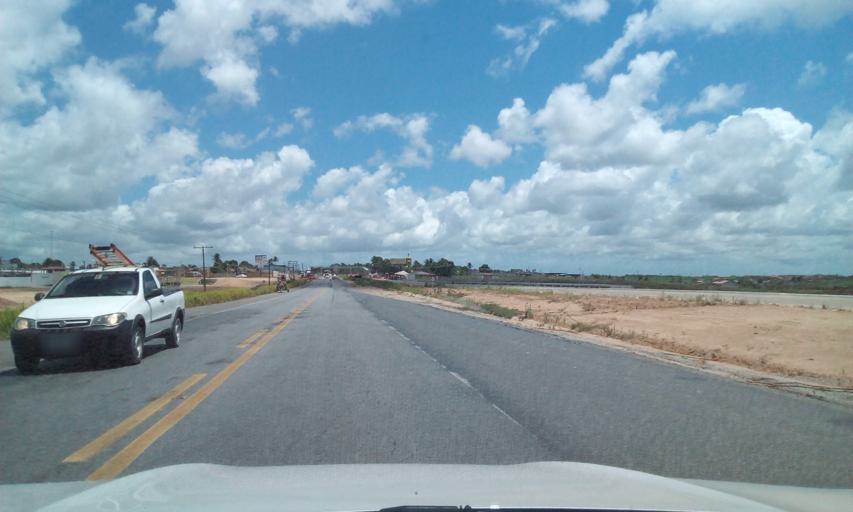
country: BR
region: Alagoas
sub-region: Campo Alegre
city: Campo Alegre
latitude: -9.9036
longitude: -36.2264
